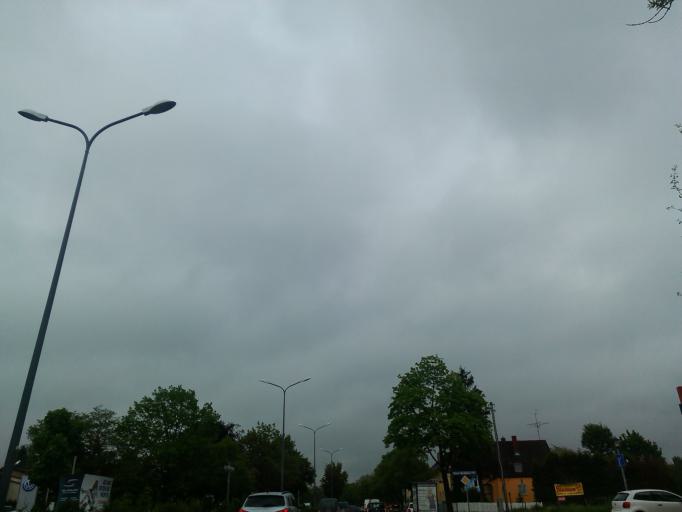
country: DE
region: Bavaria
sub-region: Upper Bavaria
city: Neubiberg
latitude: 48.1207
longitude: 11.6665
